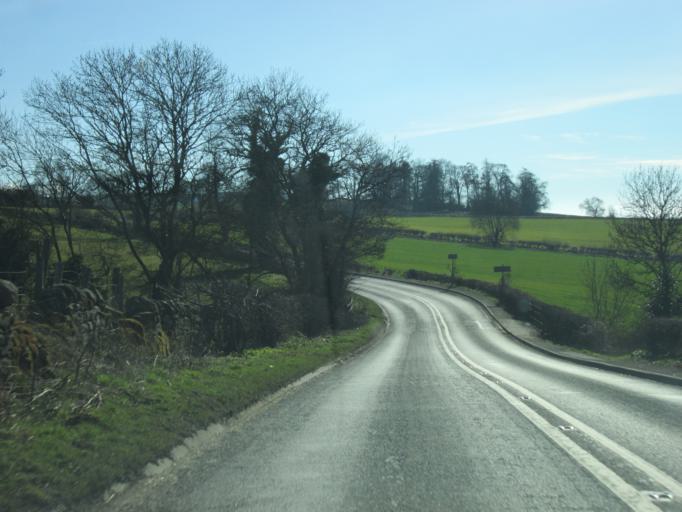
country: GB
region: England
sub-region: Northumberland
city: Wall
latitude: 55.0228
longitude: -2.1284
